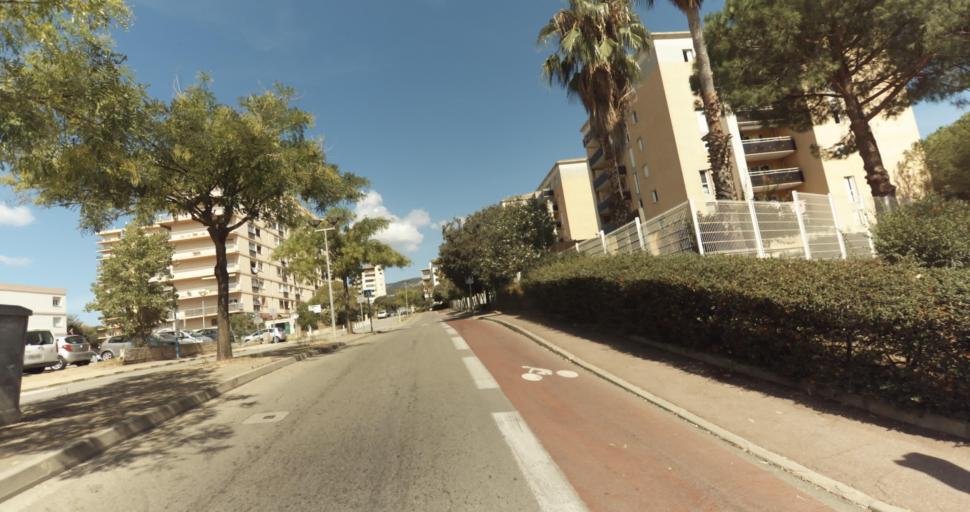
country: FR
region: Corsica
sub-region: Departement de la Corse-du-Sud
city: Ajaccio
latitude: 41.9388
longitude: 8.7509
